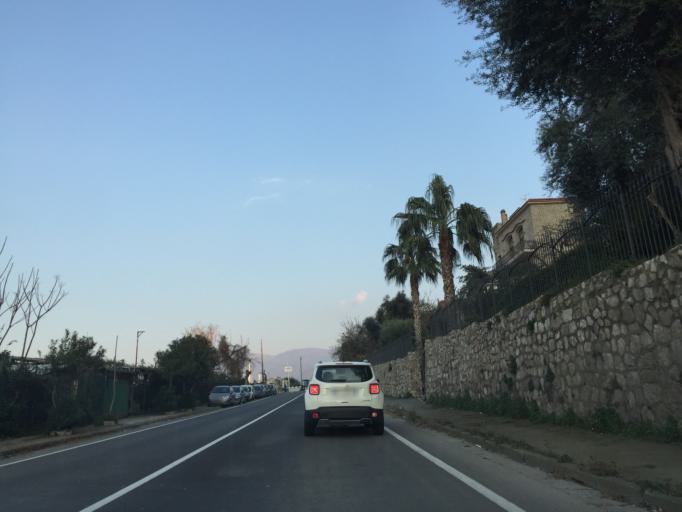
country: IT
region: Campania
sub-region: Provincia di Napoli
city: Castellammare di Stabia
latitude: 40.6888
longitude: 14.4708
